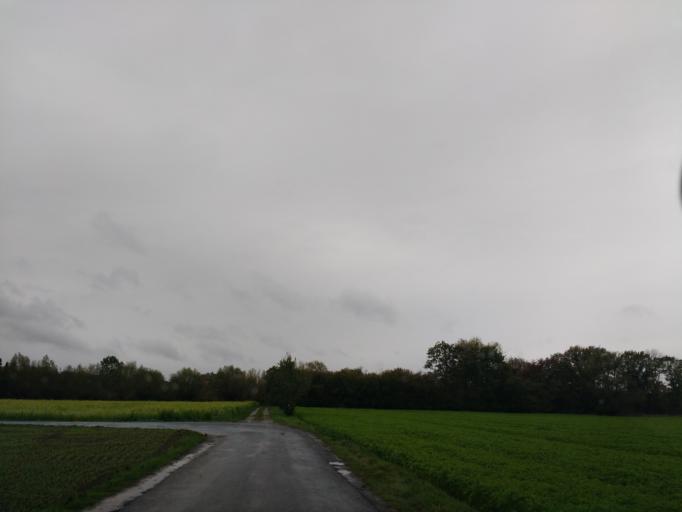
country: DE
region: North Rhine-Westphalia
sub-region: Regierungsbezirk Detmold
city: Paderborn
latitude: 51.7243
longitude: 8.6747
